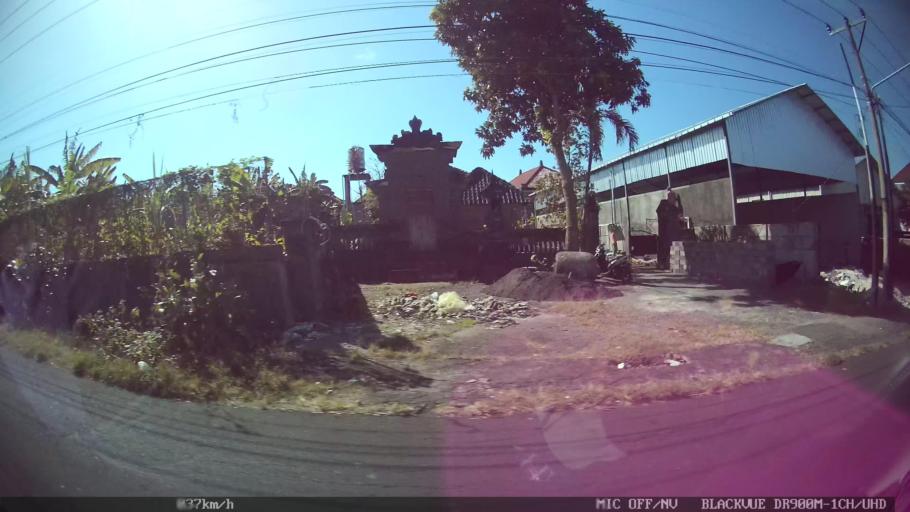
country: ID
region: Bali
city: Banjar Kertasari
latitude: -8.6333
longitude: 115.1878
